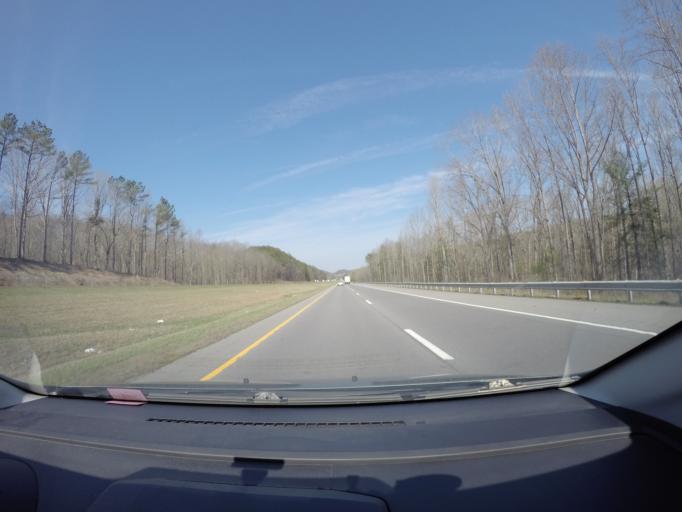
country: US
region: Tennessee
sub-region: Coffee County
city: New Union
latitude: 35.5472
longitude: -86.1862
